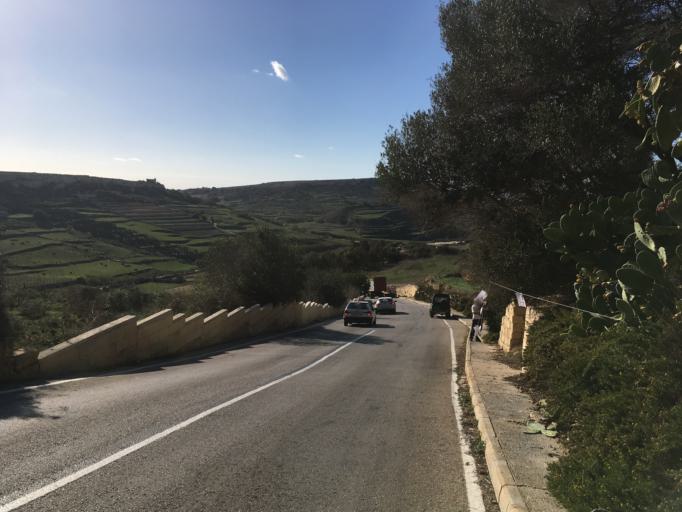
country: MT
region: L-Imgarr
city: Imgarr
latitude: 35.9199
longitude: 14.3560
